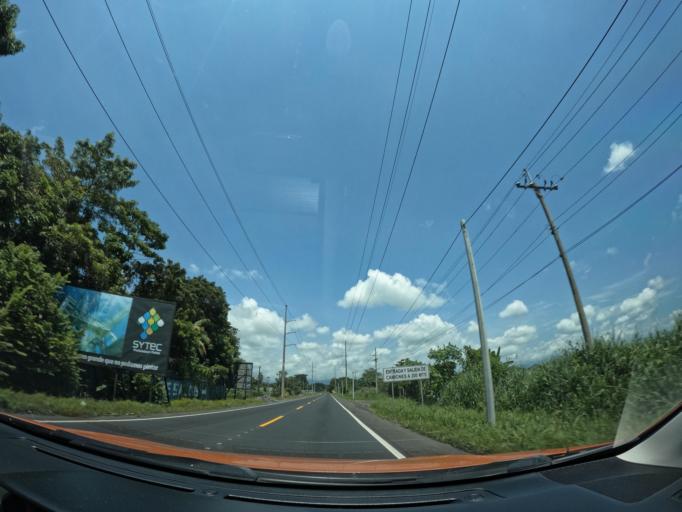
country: GT
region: Escuintla
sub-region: Municipio de Escuintla
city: Escuintla
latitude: 14.2565
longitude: -90.8004
